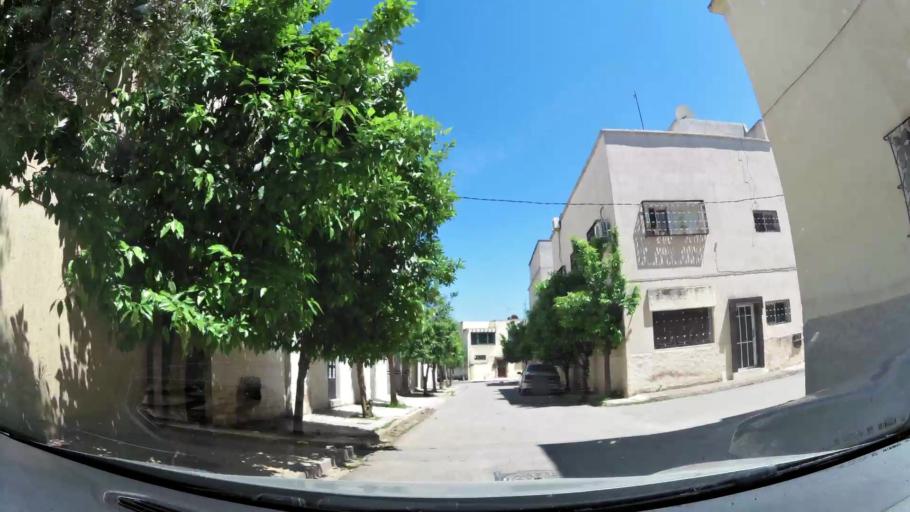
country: MA
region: Fes-Boulemane
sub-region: Fes
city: Fes
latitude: 34.0235
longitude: -5.0044
